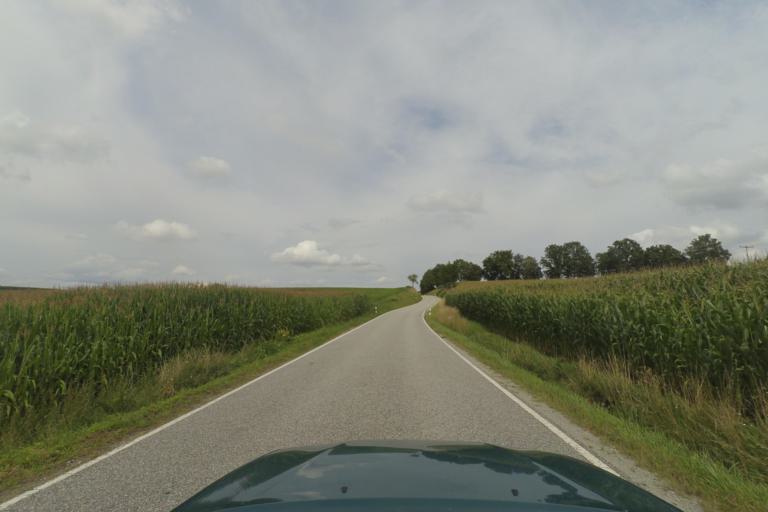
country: DE
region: Bavaria
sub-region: Lower Bavaria
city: Landau an der Isar
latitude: 48.6716
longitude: 12.7199
